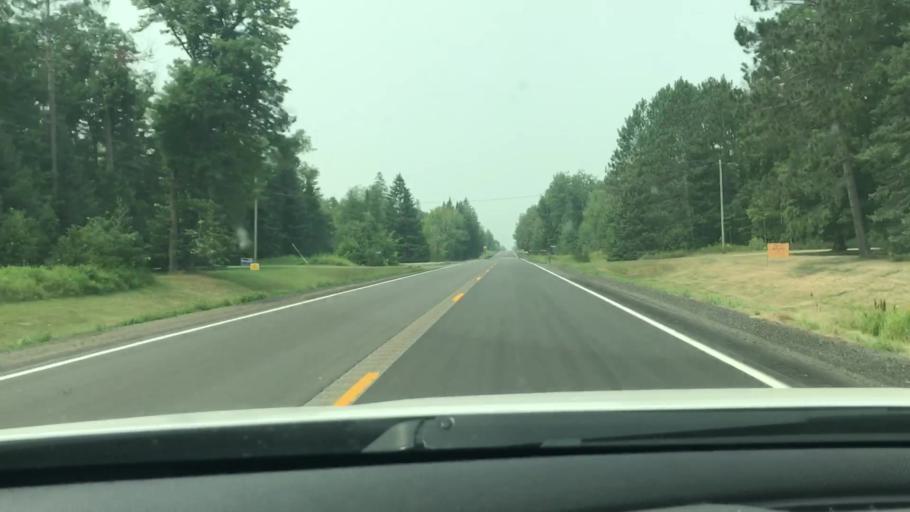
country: US
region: Minnesota
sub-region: Itasca County
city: Cohasset
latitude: 47.3571
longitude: -93.8545
